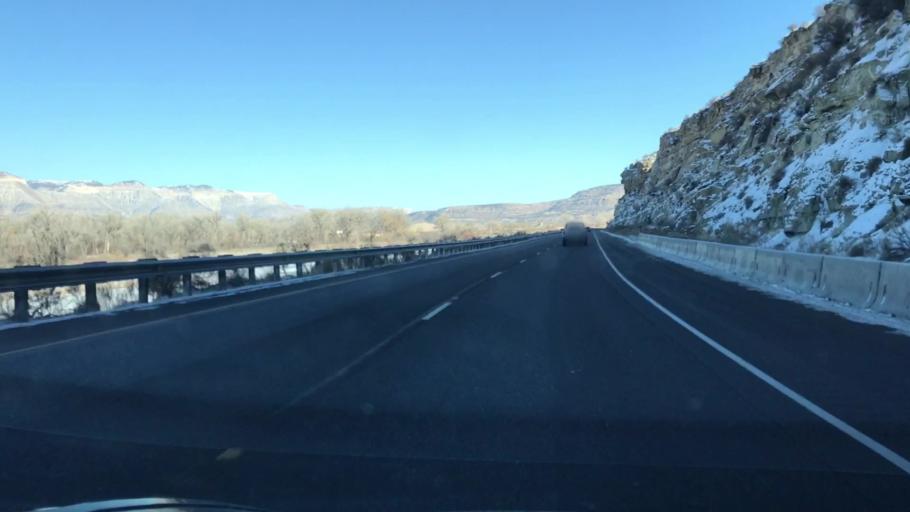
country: US
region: Colorado
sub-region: Mesa County
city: Palisade
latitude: 39.2776
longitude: -108.2406
